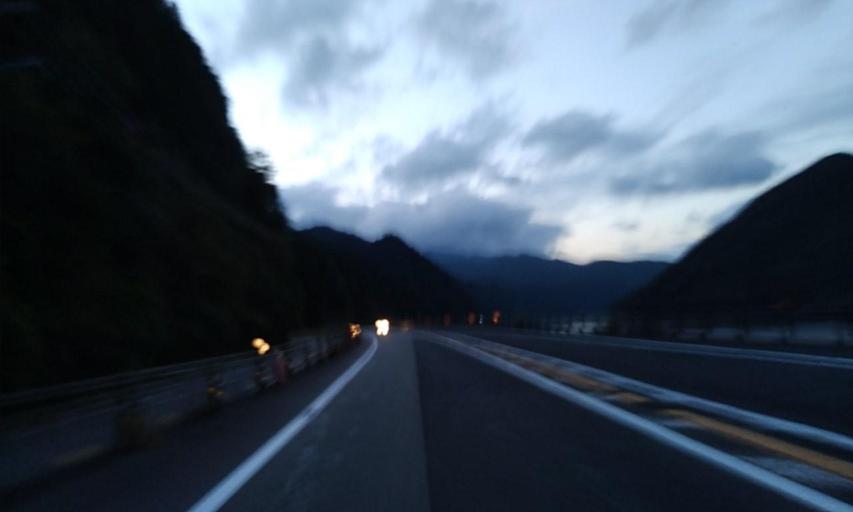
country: JP
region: Wakayama
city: Shingu
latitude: 33.7252
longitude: 135.9577
